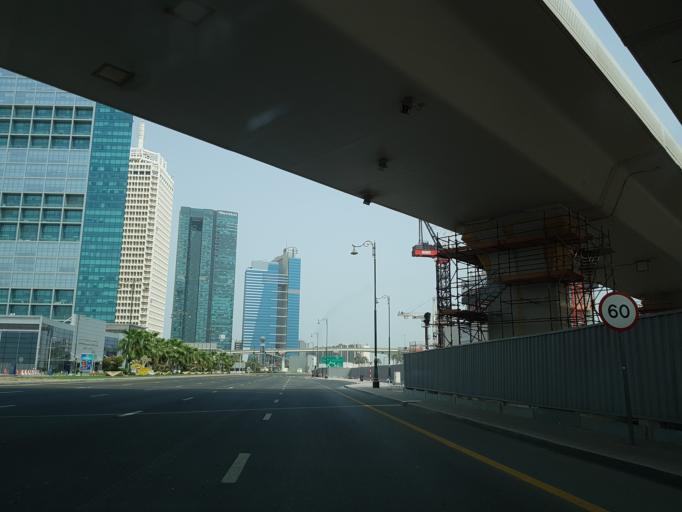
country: AE
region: Ash Shariqah
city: Sharjah
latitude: 25.2259
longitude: 55.2922
